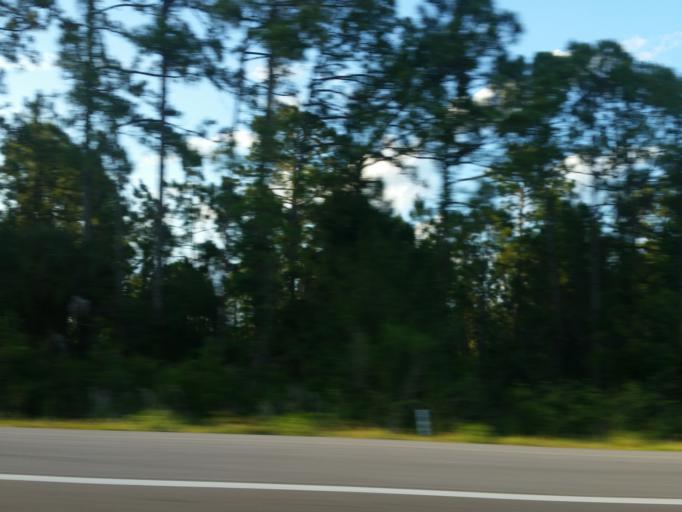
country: US
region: Florida
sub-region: Sarasota County
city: Plantation
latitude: 27.1121
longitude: -82.3166
